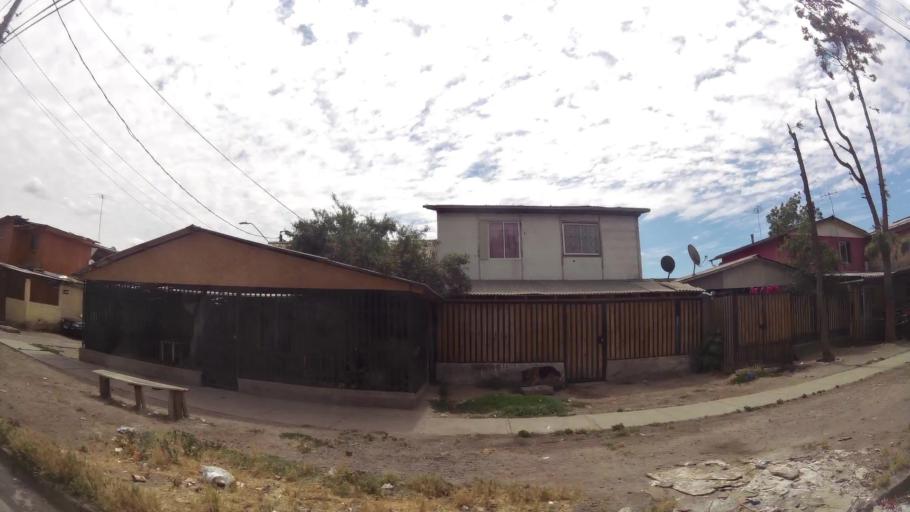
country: CL
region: Santiago Metropolitan
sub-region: Provincia de Santiago
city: La Pintana
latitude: -33.5884
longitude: -70.6643
